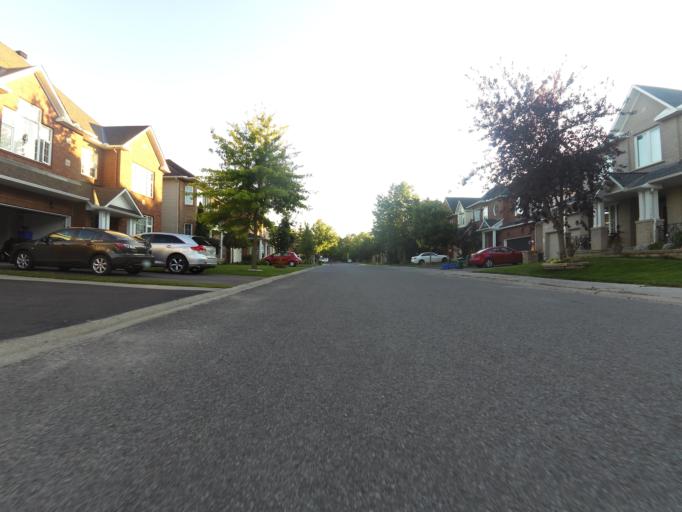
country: CA
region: Ontario
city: Bells Corners
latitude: 45.2796
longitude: -75.7069
